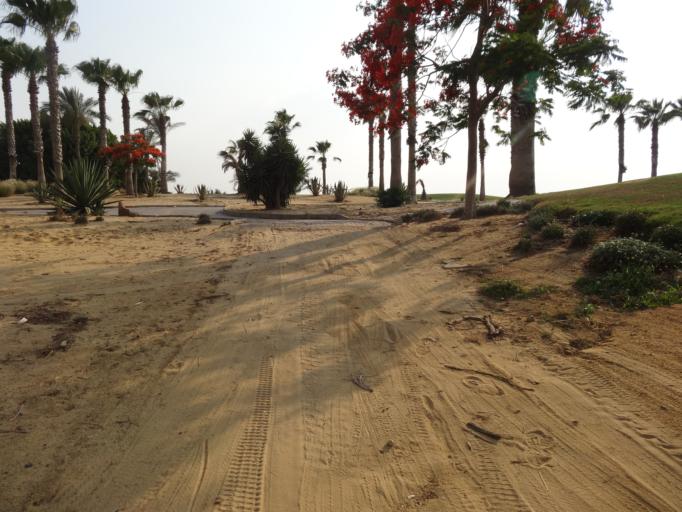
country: EG
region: Muhafazat al Qalyubiyah
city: Al Khankah
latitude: 30.0689
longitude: 31.4353
